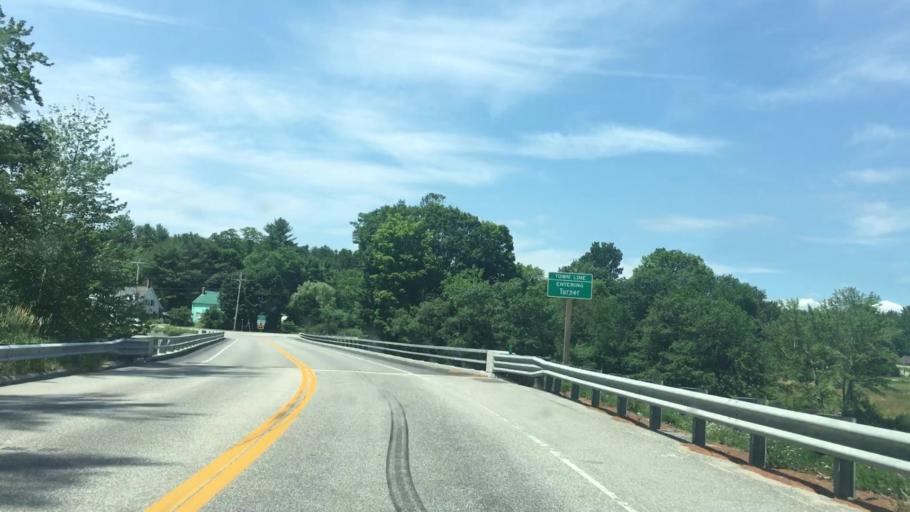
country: US
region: Maine
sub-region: Androscoggin County
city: Livermore
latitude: 44.3425
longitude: -70.1877
